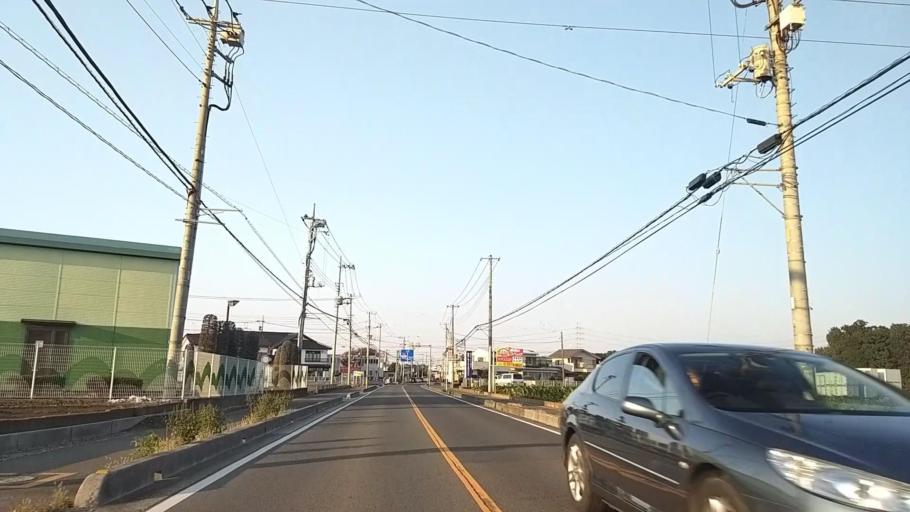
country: JP
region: Saitama
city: Tokorozawa
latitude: 35.8328
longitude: 139.4649
